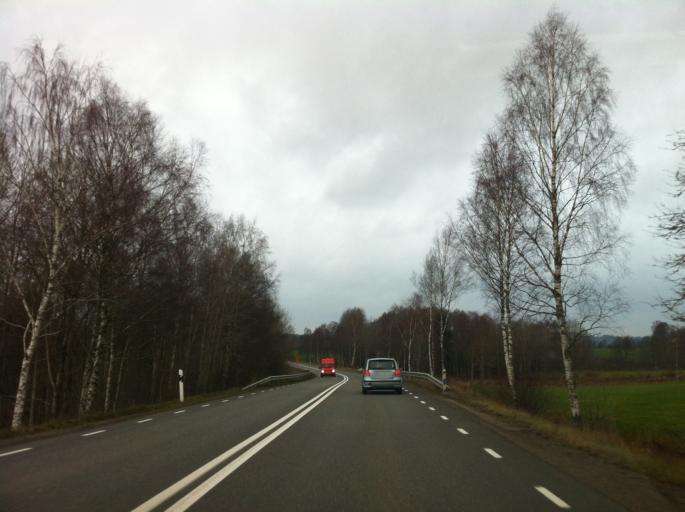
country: SE
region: Joenkoeping
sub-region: Vetlanda Kommun
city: Landsbro
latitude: 57.4035
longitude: 14.9414
